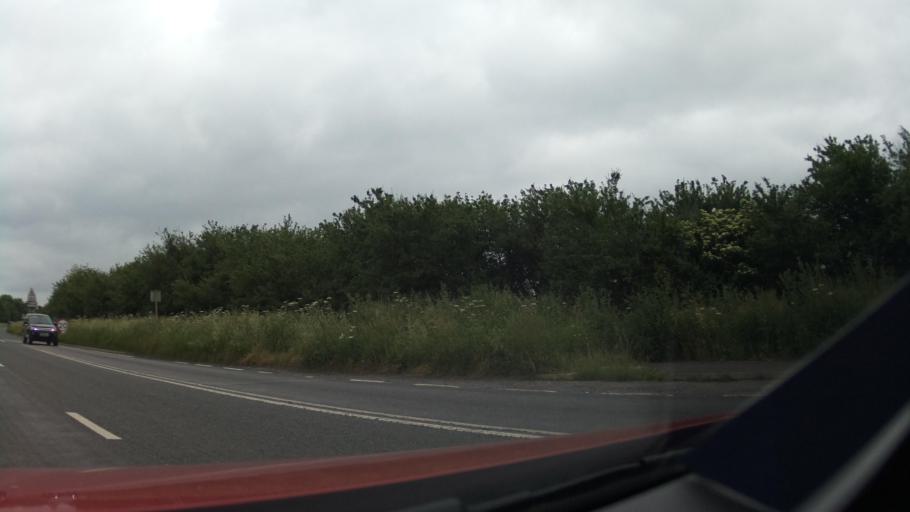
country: GB
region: England
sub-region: District of Rutland
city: Ridlington
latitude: 52.5980
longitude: -0.7578
